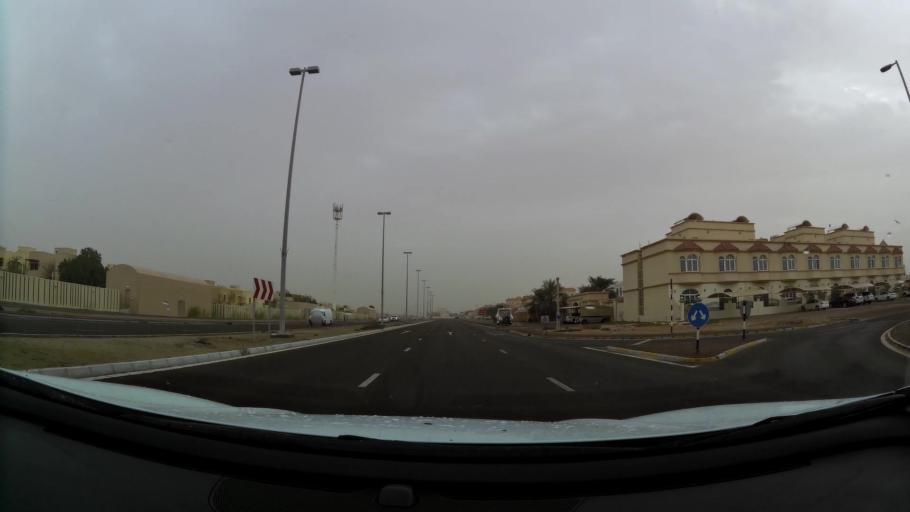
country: AE
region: Abu Dhabi
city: Abu Dhabi
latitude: 24.4354
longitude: 54.5841
